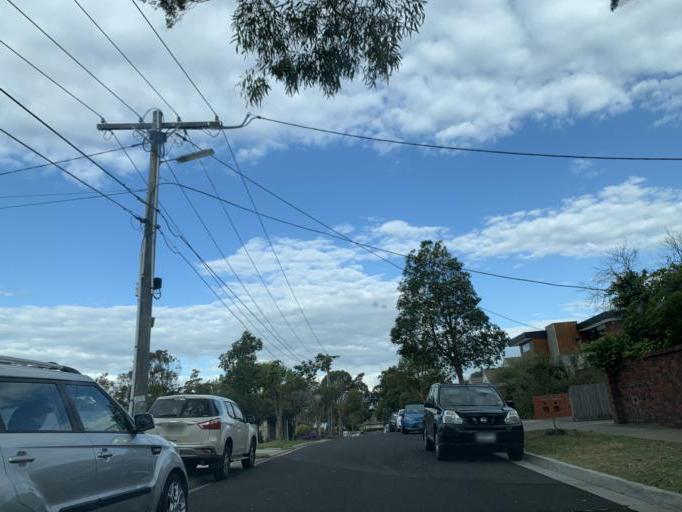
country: AU
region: Victoria
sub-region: Bayside
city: Hampton
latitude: -37.9471
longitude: 145.0149
